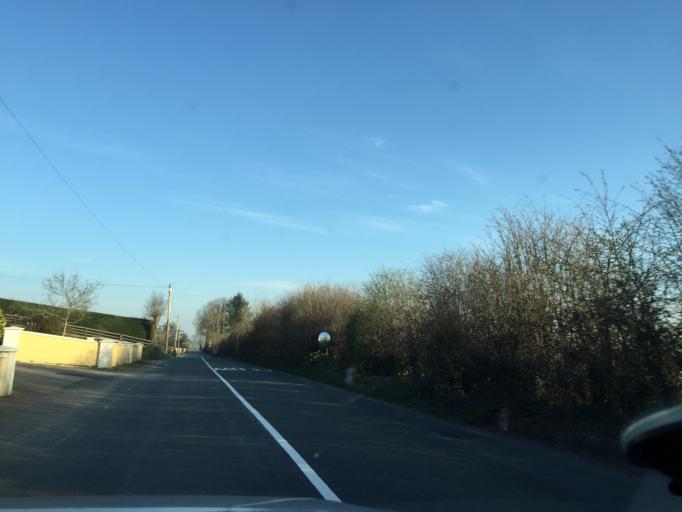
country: IE
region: Munster
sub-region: Ciarrai
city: Cill Airne
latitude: 52.0851
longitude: -9.5267
